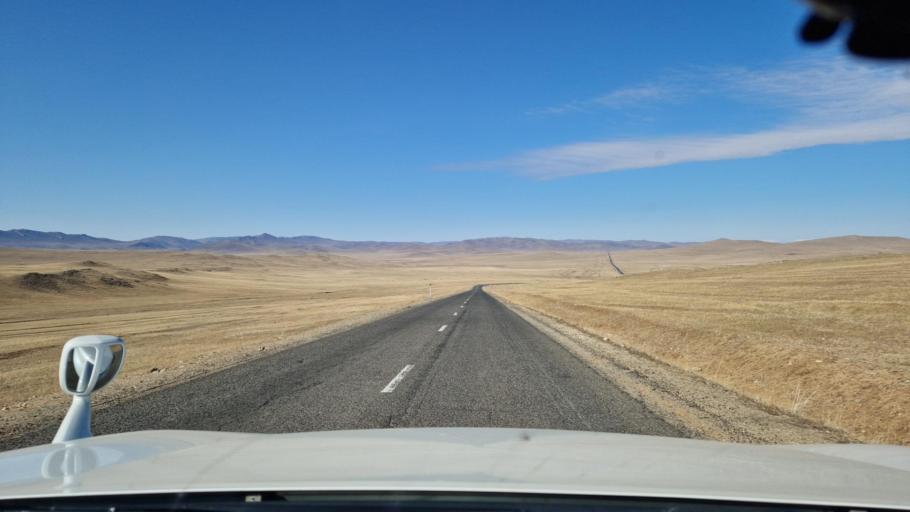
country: MN
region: Hentiy
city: Modot
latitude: 47.5910
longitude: 109.2668
